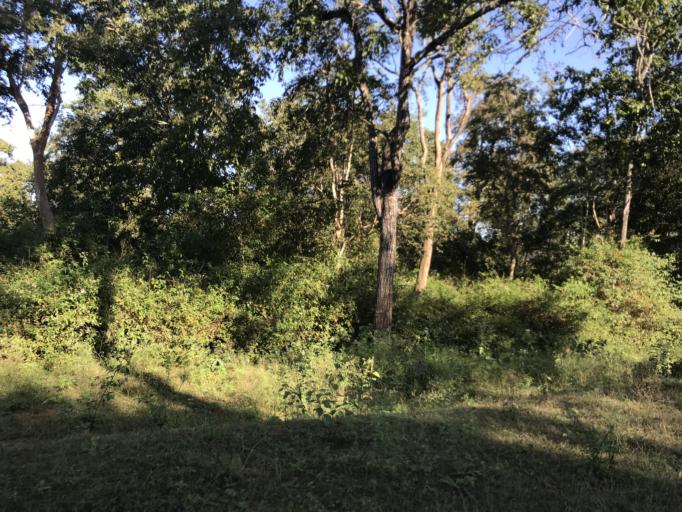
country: IN
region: Karnataka
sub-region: Mysore
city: Heggadadevankote
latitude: 11.9697
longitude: 76.2447
